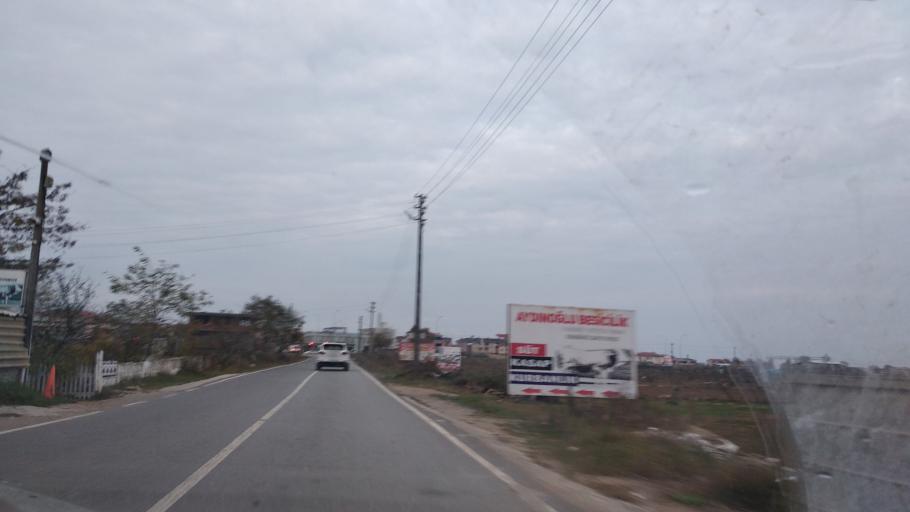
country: TR
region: Sakarya
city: Karasu
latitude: 41.0857
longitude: 30.7398
